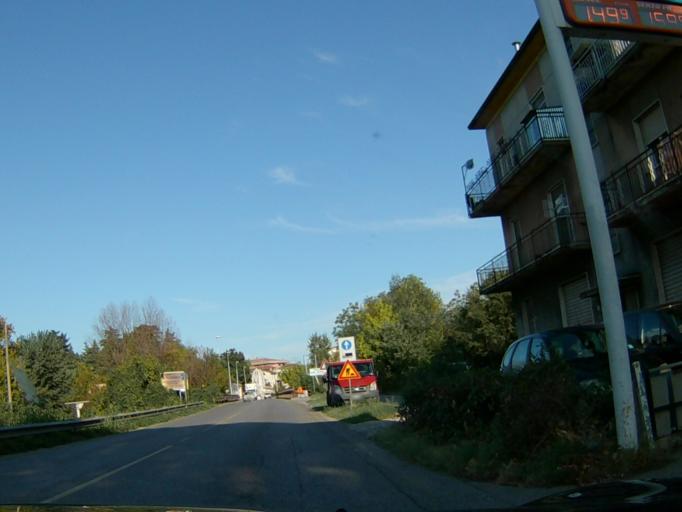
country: IT
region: Lombardy
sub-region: Provincia di Brescia
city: Ponte San Marco
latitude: 45.4755
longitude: 10.4054
